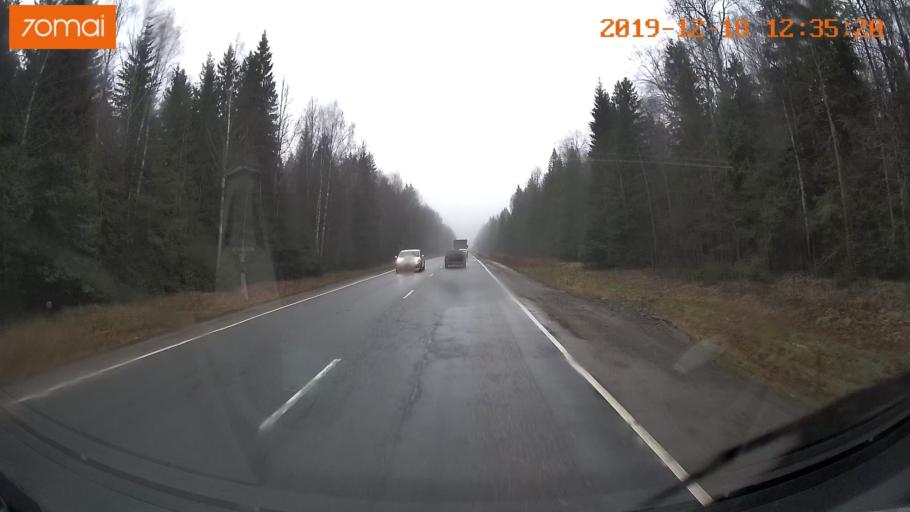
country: RU
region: Moskovskaya
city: Rumyantsevo
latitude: 56.1283
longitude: 36.5817
